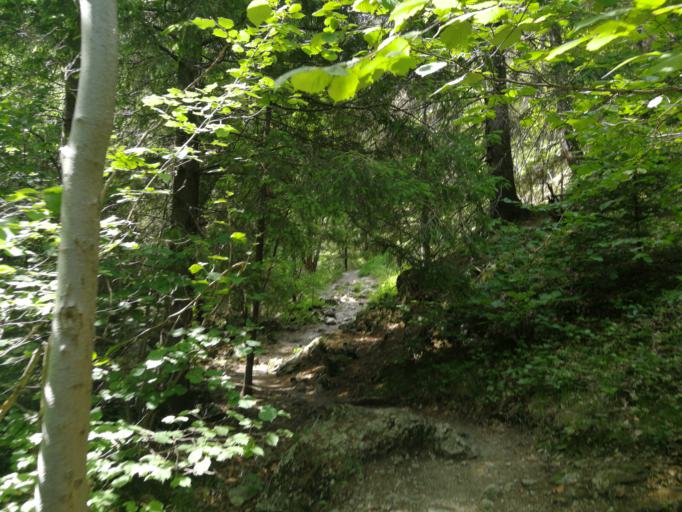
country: SK
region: Zilinsky
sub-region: Okres Liptovsky Mikulas
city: Liptovsky Mikulas
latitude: 49.1782
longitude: 19.4871
